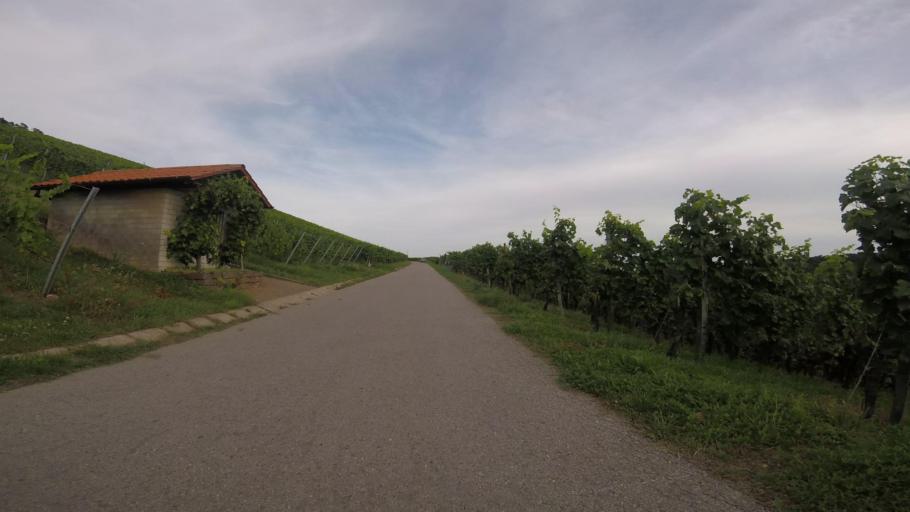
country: DE
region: Baden-Wuerttemberg
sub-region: Regierungsbezirk Stuttgart
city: Grossbottwar
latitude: 48.9926
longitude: 9.3100
